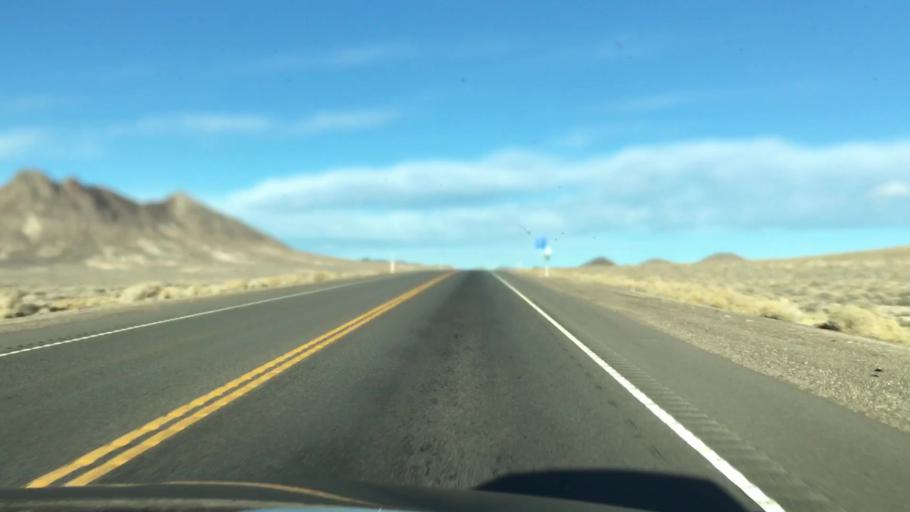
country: US
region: Nevada
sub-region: Nye County
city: Tonopah
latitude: 38.0228
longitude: -117.2426
